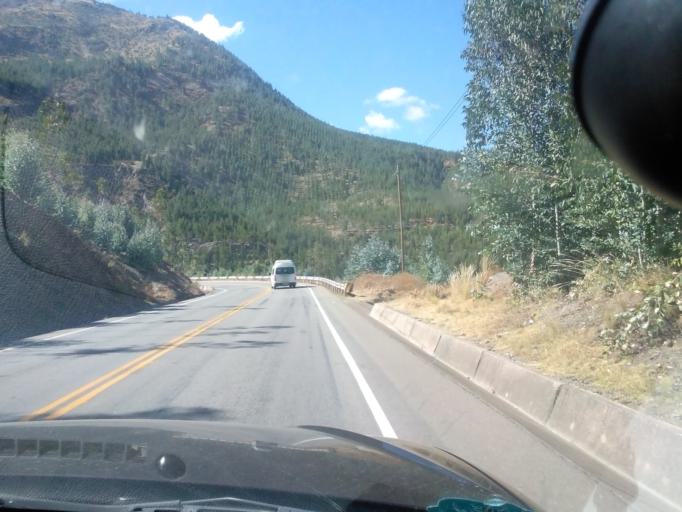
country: PE
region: Cusco
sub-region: Provincia de Quispicanchis
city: Urcos
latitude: -13.6878
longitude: -71.5973
